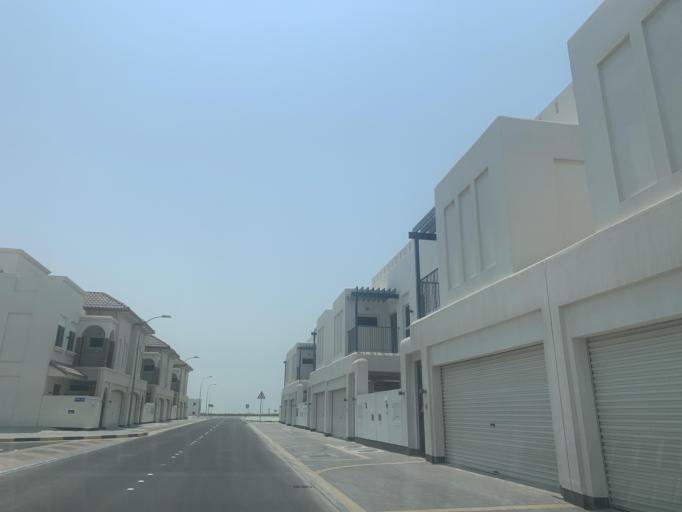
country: BH
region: Muharraq
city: Al Muharraq
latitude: 26.3143
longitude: 50.6246
